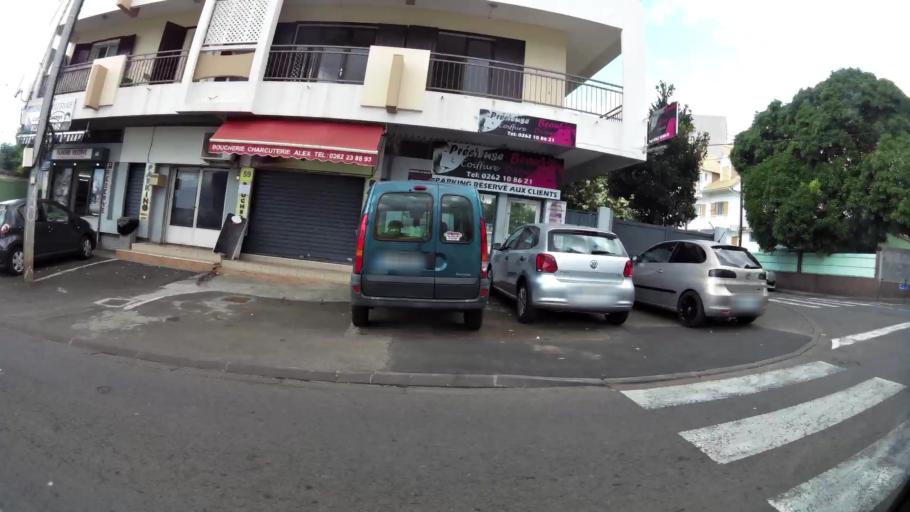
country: RE
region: Reunion
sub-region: Reunion
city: Saint-Denis
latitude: -20.8949
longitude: 55.4817
